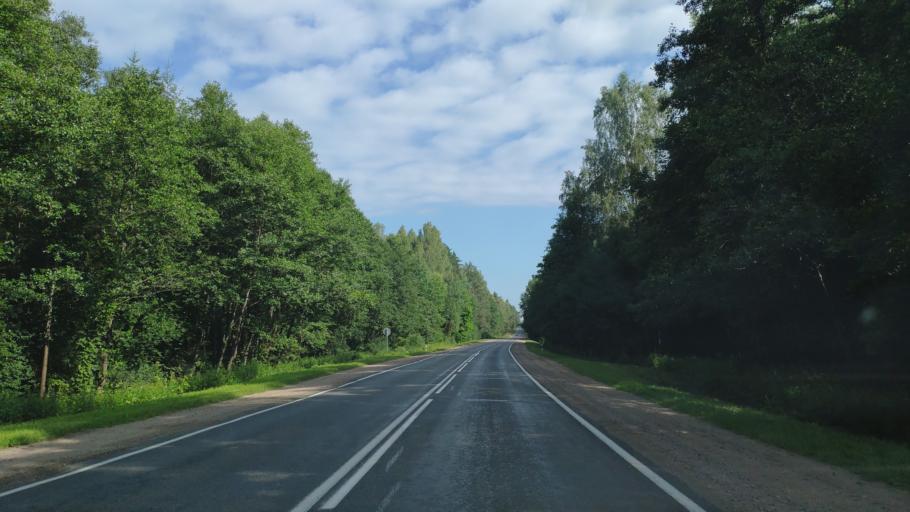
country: BY
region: Minsk
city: Novosel'ye
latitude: 53.9315
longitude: 27.2434
